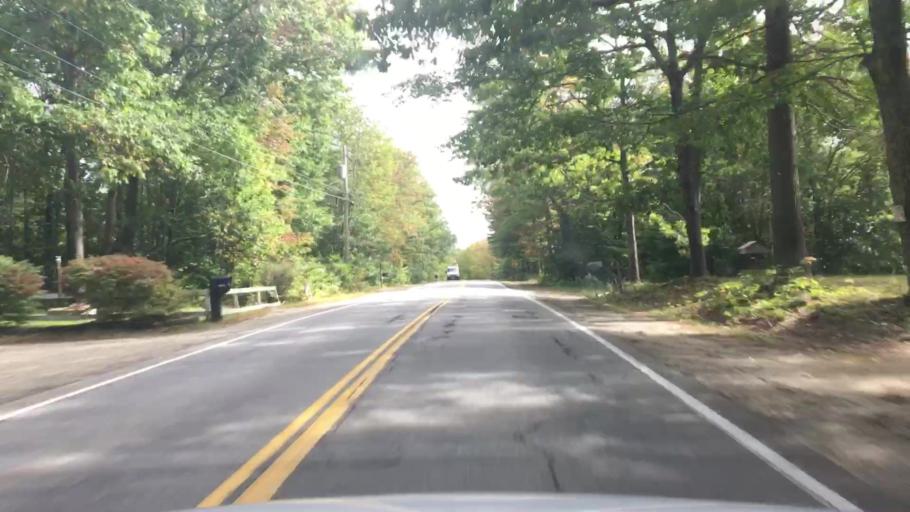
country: US
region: Maine
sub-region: Androscoggin County
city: Lisbon Falls
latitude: 43.9563
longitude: -70.0448
